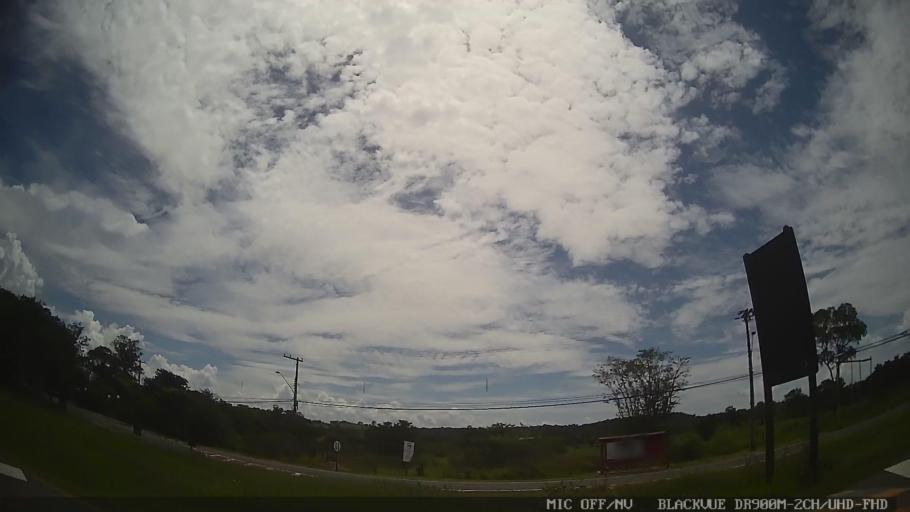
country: BR
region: Sao Paulo
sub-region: Conchas
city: Conchas
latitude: -23.0674
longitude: -47.9745
